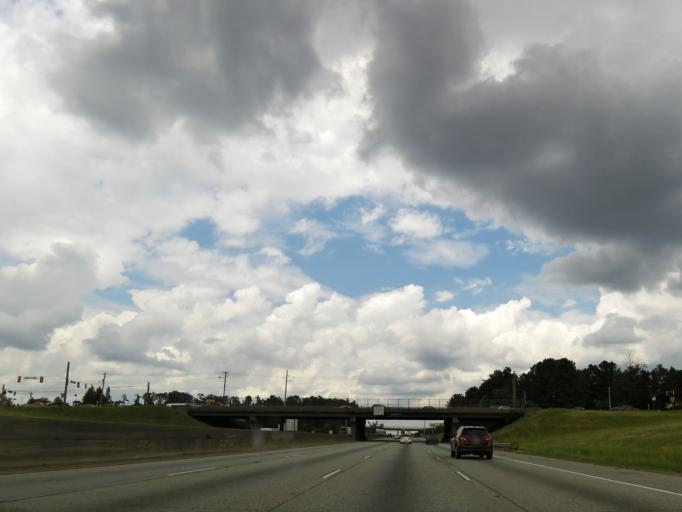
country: US
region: Georgia
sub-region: Fulton County
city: College Park
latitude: 33.6552
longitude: -84.4975
